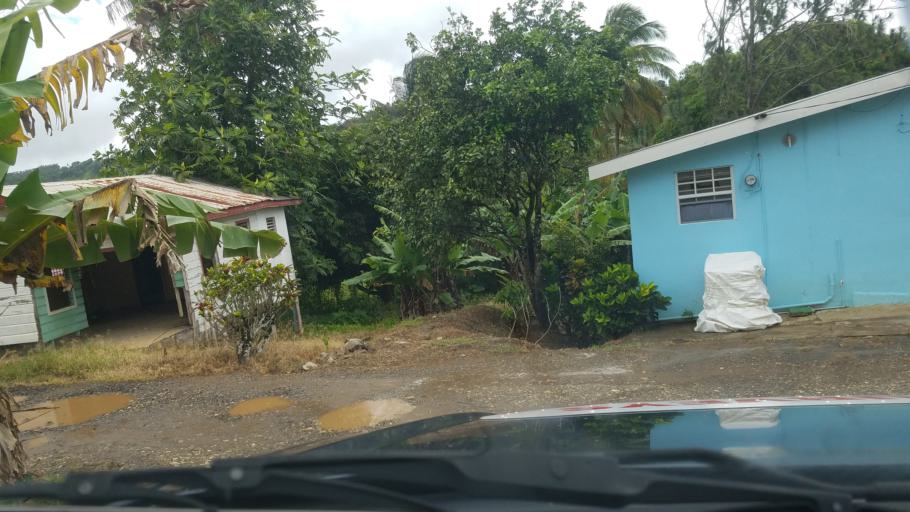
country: LC
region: Castries Quarter
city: Bisee
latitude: 13.9951
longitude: -60.9559
